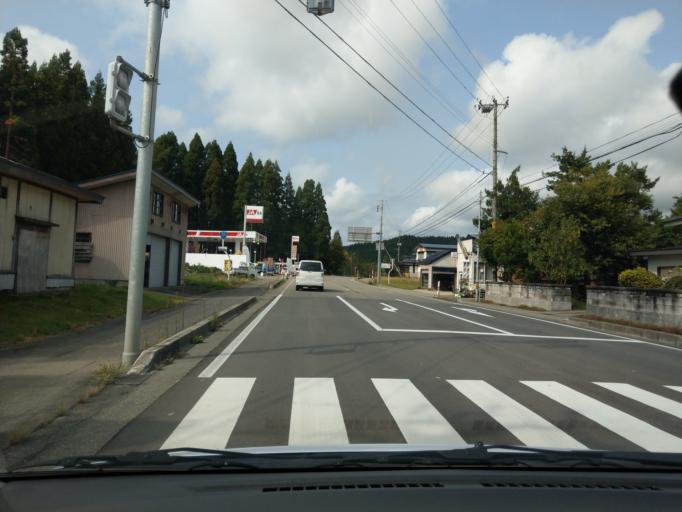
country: JP
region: Akita
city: Omagari
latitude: 39.4394
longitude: 140.3584
